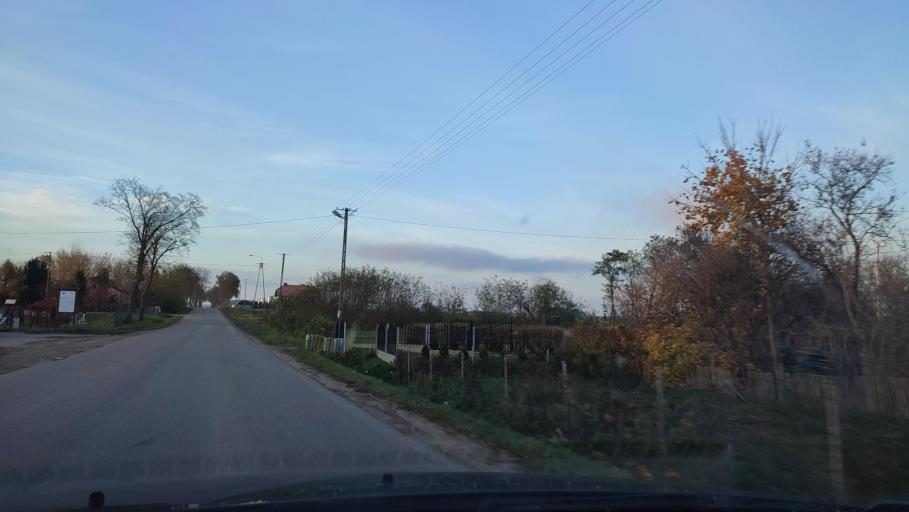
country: PL
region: Masovian Voivodeship
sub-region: Powiat mlawski
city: Wieczfnia Koscielna
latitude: 53.1900
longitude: 20.4394
